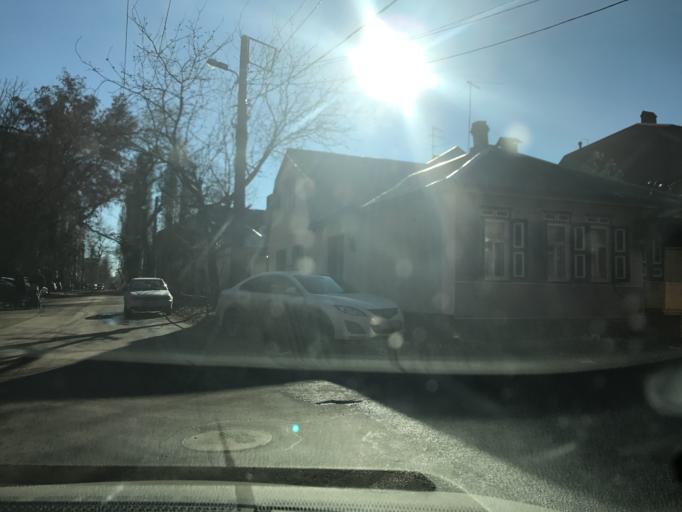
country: RU
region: Rostov
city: Rostov-na-Donu
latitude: 47.2399
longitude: 39.7569
